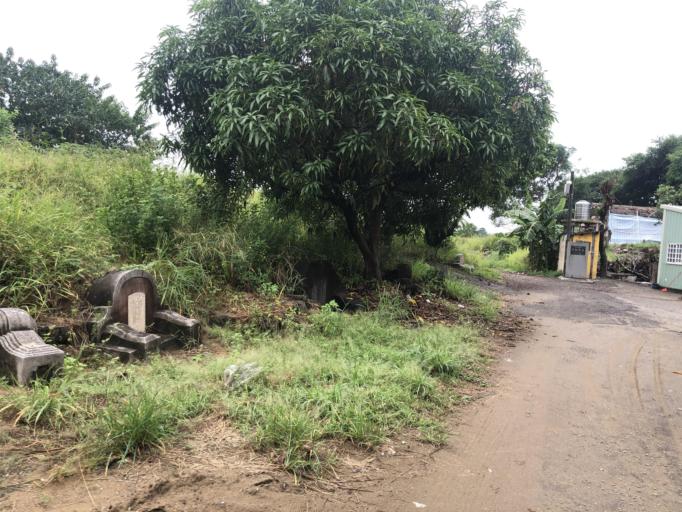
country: TW
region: Taiwan
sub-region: Tainan
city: Tainan
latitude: 22.9672
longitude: 120.1989
